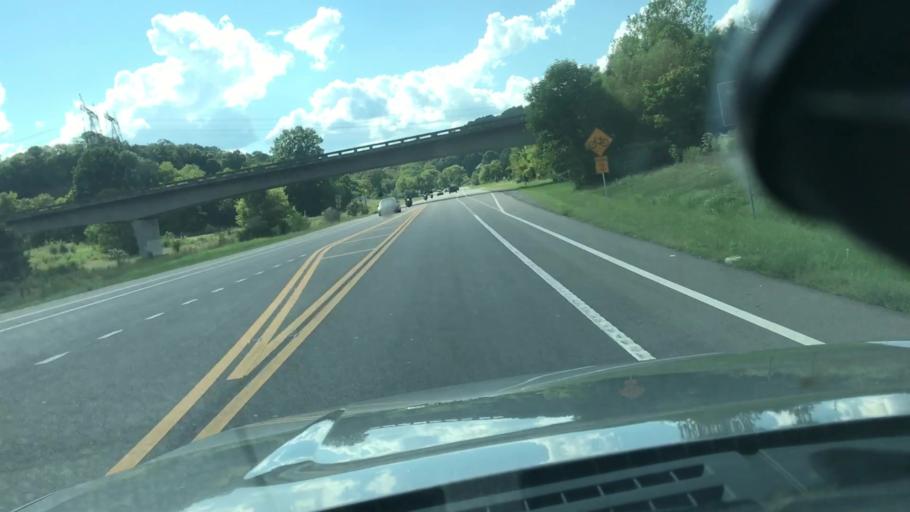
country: US
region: Tennessee
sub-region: Cheatham County
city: Pegram
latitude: 36.0345
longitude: -86.9746
